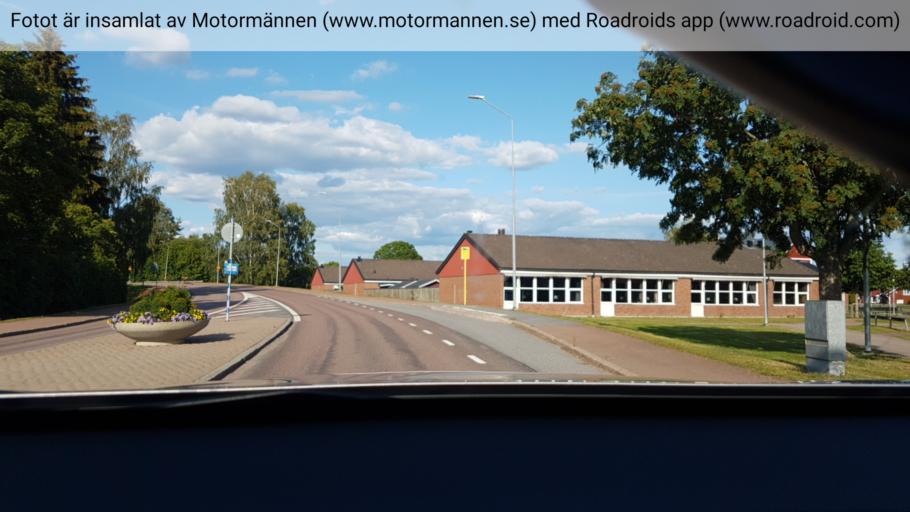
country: SE
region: Vaermland
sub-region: Forshaga Kommun
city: Forshaga
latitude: 59.5208
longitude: 13.4835
